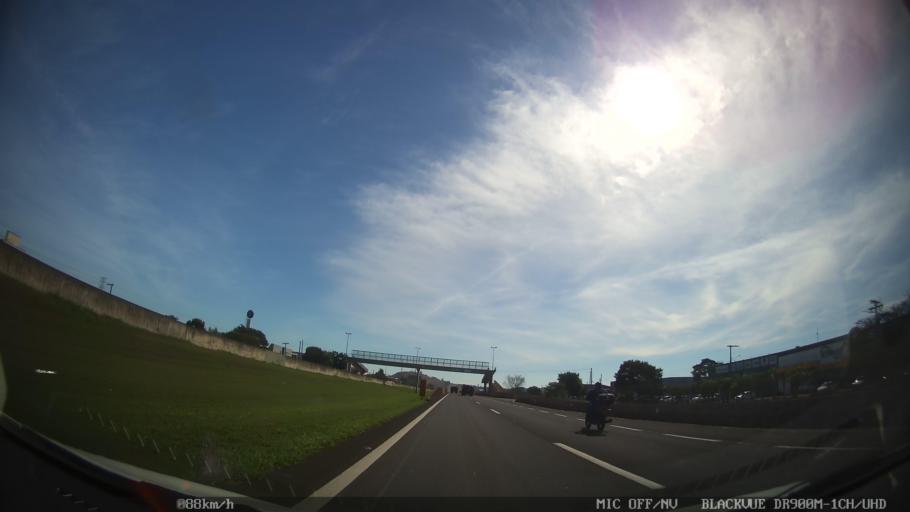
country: BR
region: Sao Paulo
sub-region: Leme
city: Leme
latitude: -22.1816
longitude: -47.3982
